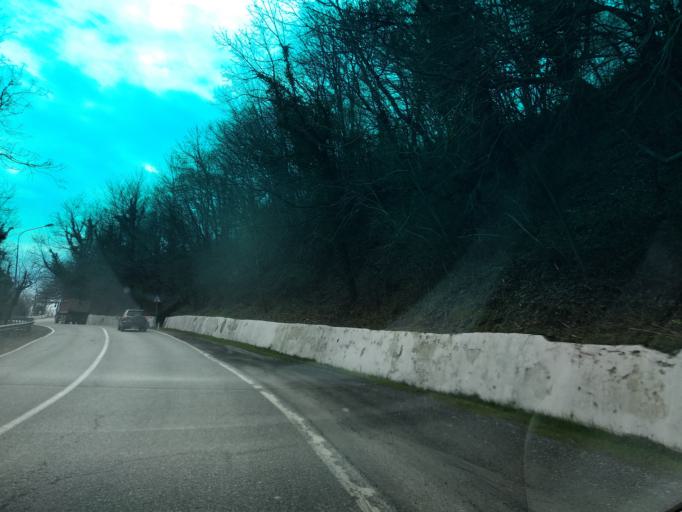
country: RU
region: Krasnodarskiy
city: Shepsi
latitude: 44.0594
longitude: 39.1333
